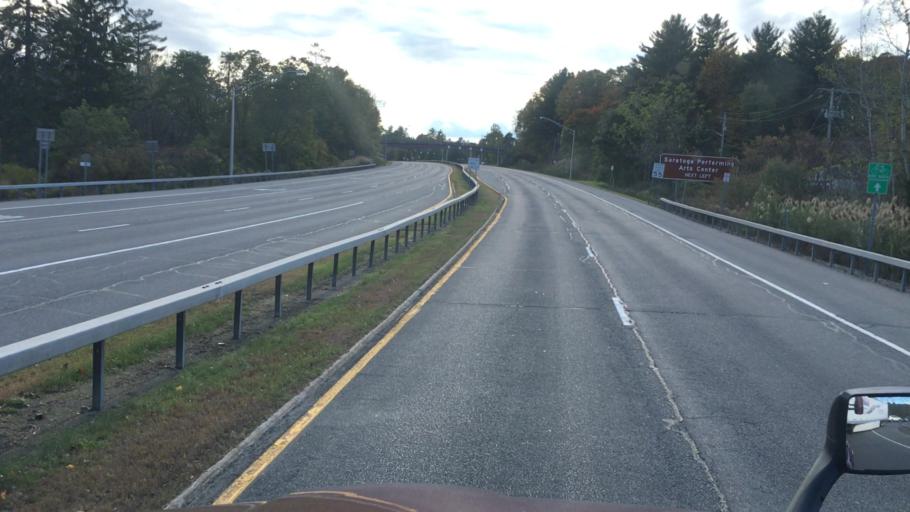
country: US
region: New York
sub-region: Saratoga County
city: Saratoga Springs
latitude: 43.0577
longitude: -73.8079
